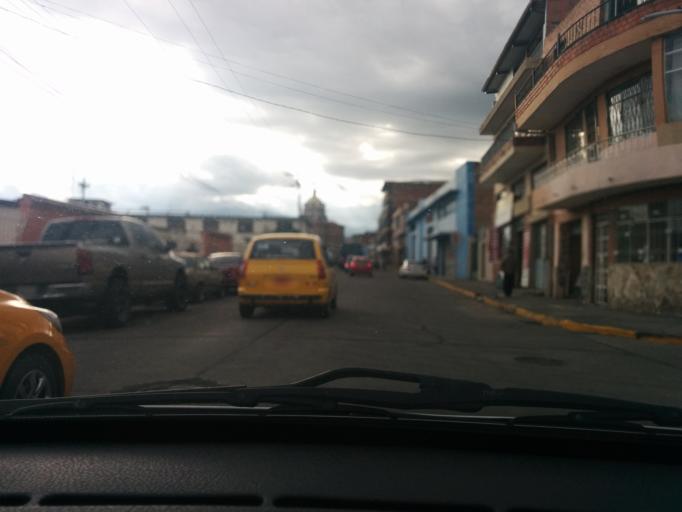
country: EC
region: Azuay
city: Cuenca
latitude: -2.8989
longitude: -78.9952
